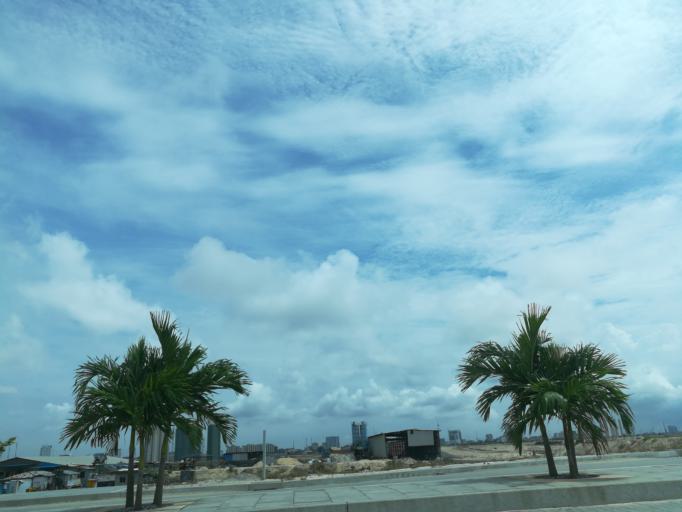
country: NG
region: Lagos
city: Lagos
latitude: 6.4095
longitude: 3.4082
